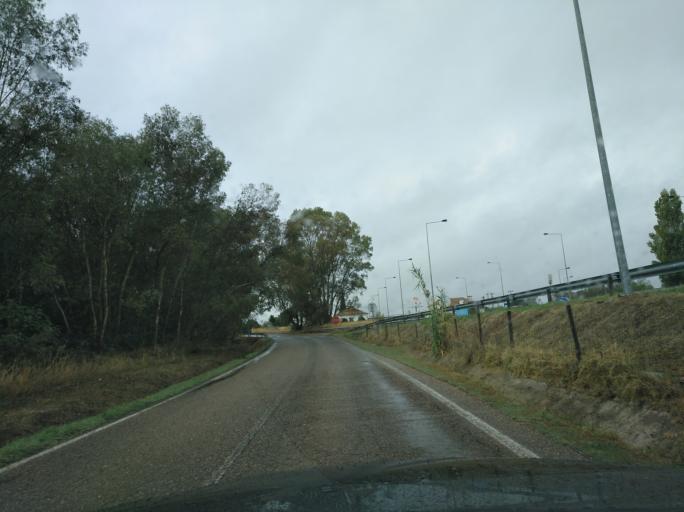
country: ES
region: Extremadura
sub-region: Provincia de Badajoz
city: Badajoz
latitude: 38.8827
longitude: -7.0443
